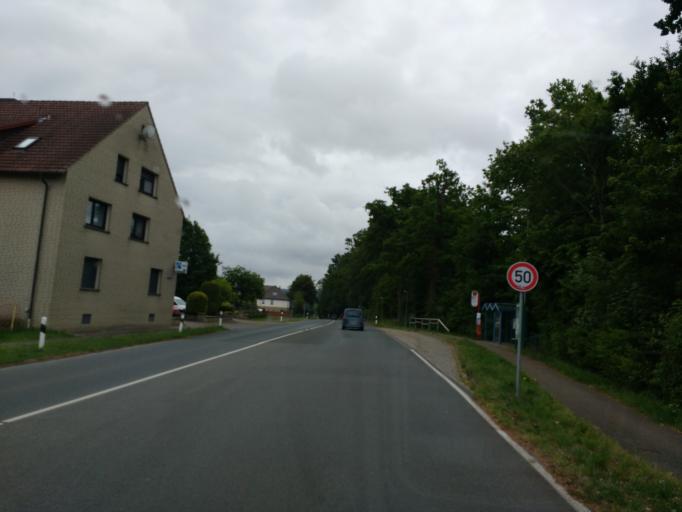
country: DE
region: Lower Saxony
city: Hilter
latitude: 52.1849
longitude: 8.1386
